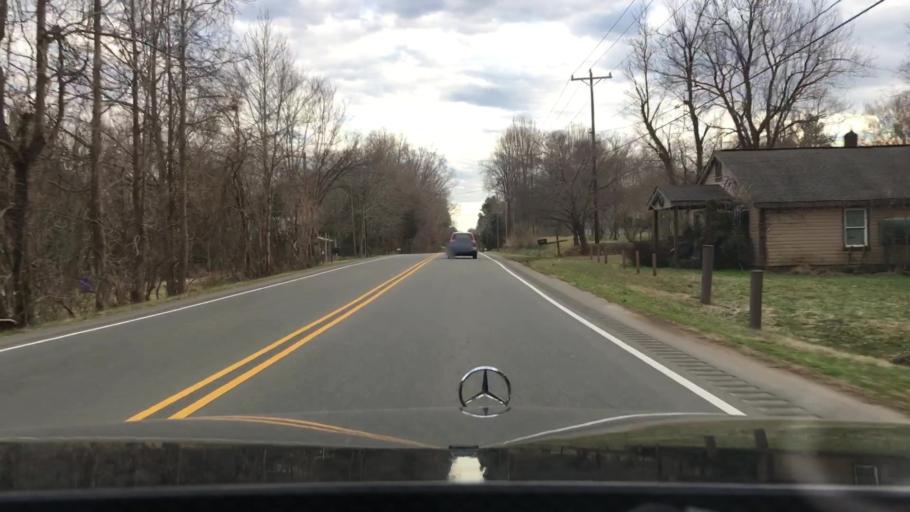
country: US
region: North Carolina
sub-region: Orange County
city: Hillsborough
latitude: 36.1186
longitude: -79.1140
